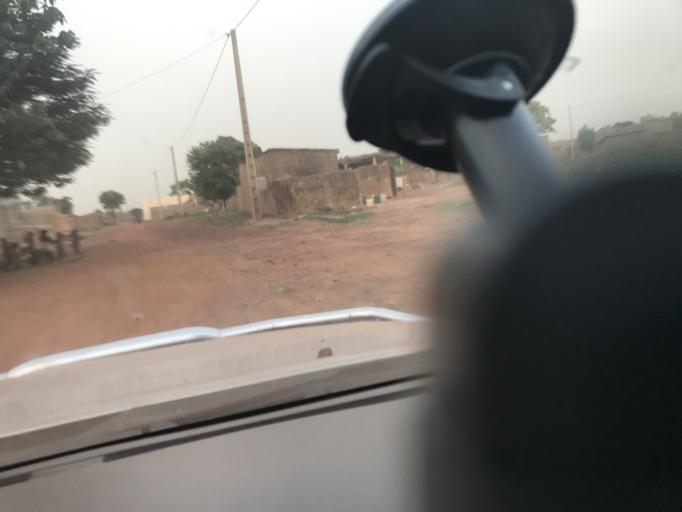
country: ML
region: Bamako
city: Bamako
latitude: 12.6520
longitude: -7.8833
